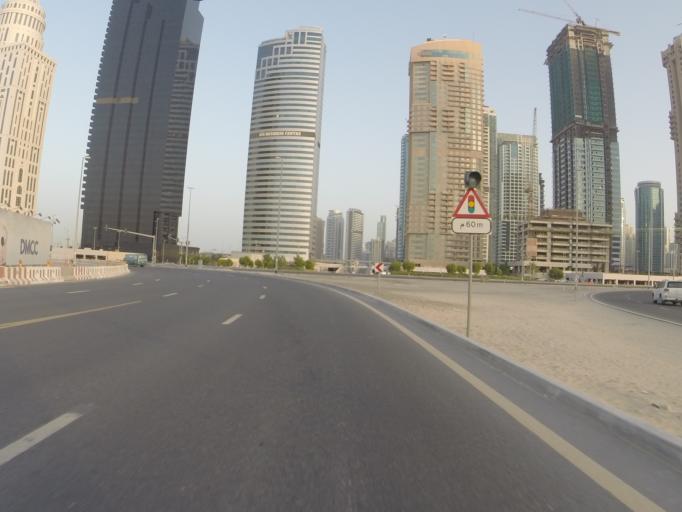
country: AE
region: Dubai
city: Dubai
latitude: 25.0629
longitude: 55.1406
